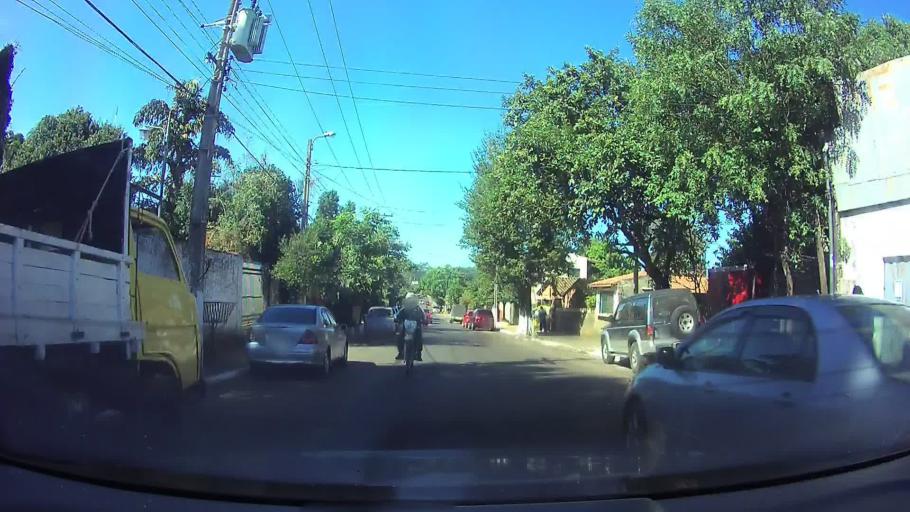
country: PY
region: Central
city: Villa Elisa
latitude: -25.3484
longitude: -57.5806
